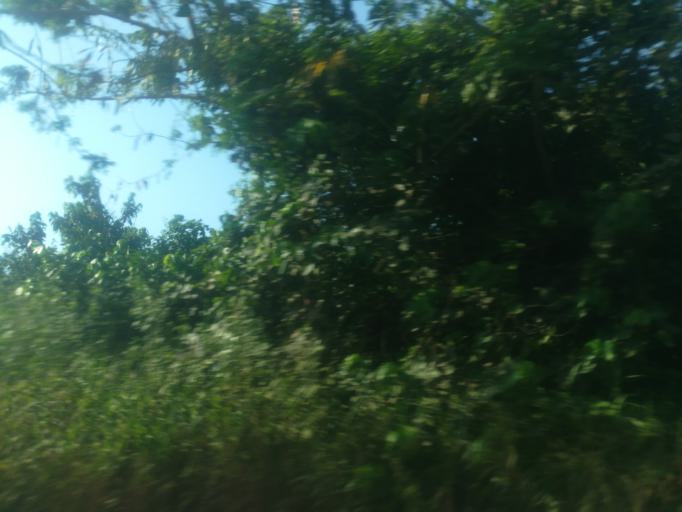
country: NG
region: Ogun
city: Abeokuta
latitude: 7.1411
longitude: 3.2521
